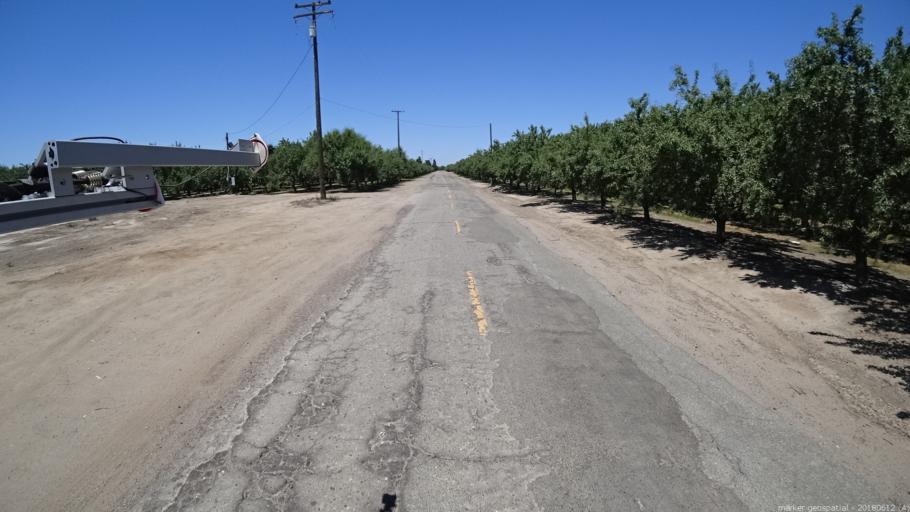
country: US
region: California
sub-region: Madera County
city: Chowchilla
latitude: 37.0777
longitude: -120.2659
